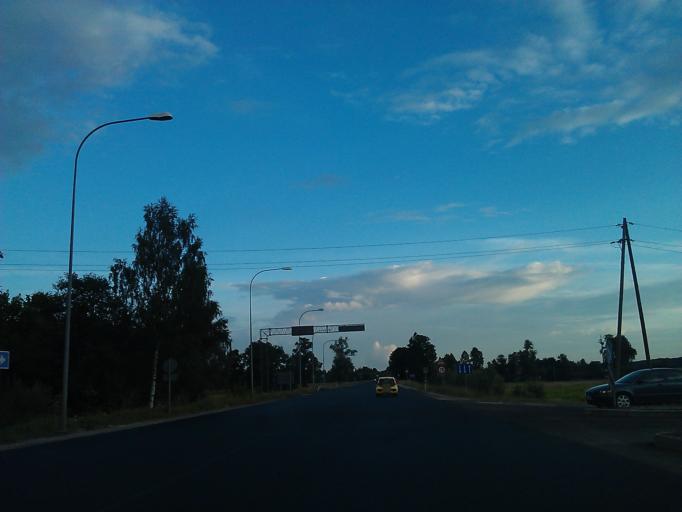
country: LV
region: Adazi
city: Adazi
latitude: 57.1180
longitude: 24.3241
